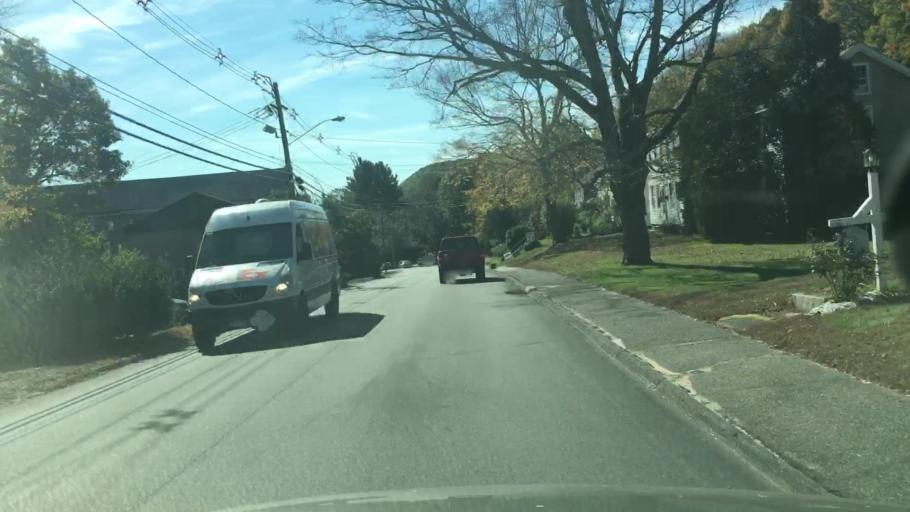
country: US
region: Connecticut
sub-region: Tolland County
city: Stafford Springs
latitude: 41.9581
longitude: -72.3019
